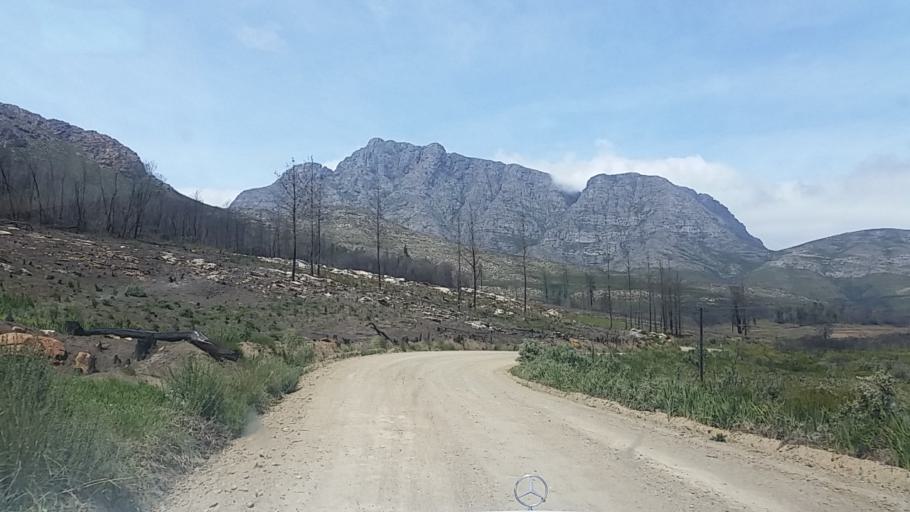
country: ZA
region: Western Cape
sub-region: Eden District Municipality
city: George
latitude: -33.8658
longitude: 22.4471
